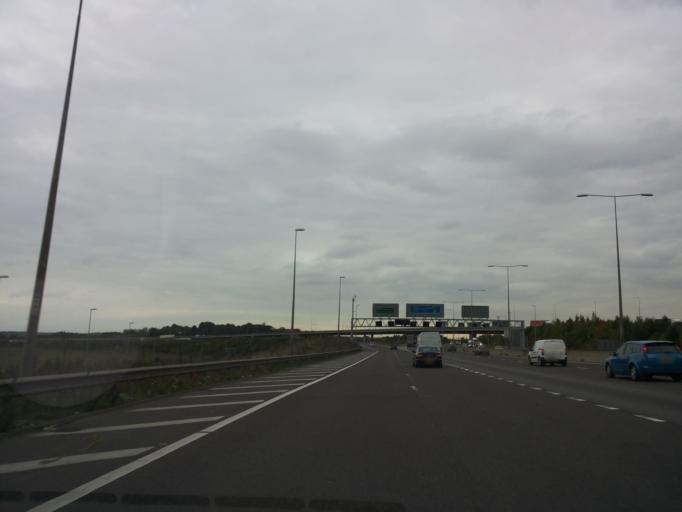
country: GB
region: England
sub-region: Kent
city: Dartford
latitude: 51.4321
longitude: 0.2394
